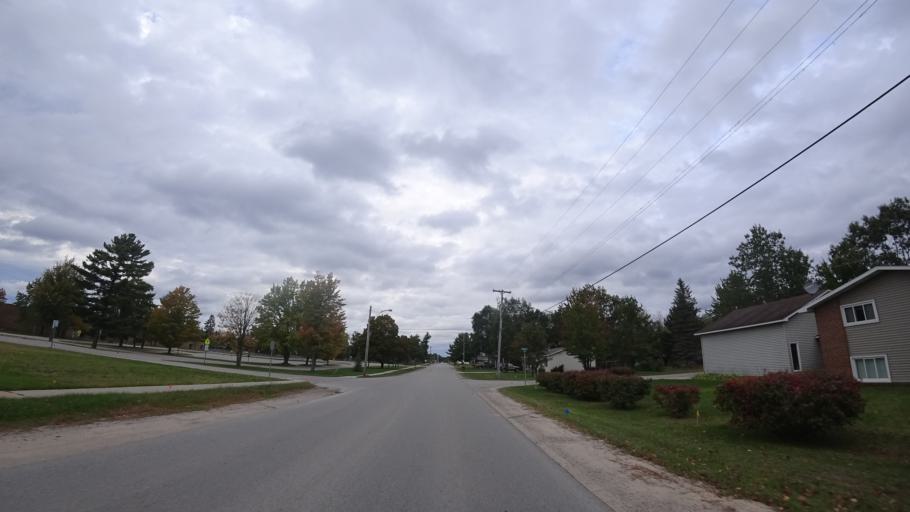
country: US
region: Michigan
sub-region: Kalkaska County
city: Kalkaska
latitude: 44.7369
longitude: -85.1846
